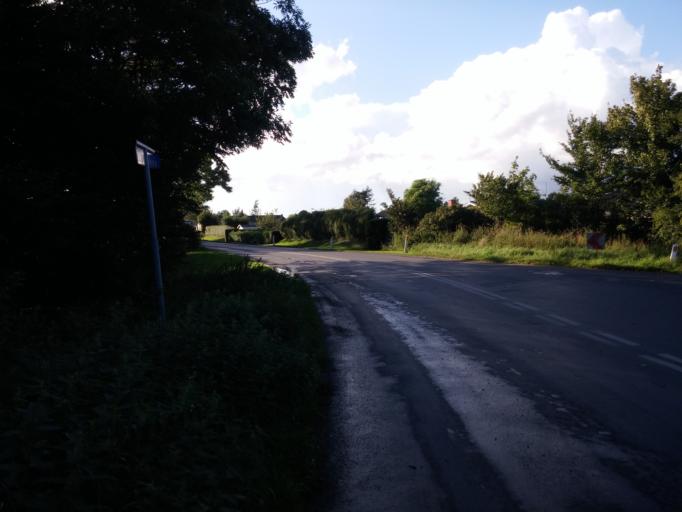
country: DK
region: Zealand
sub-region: Kalundborg Kommune
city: Svebolle
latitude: 55.7497
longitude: 11.3381
